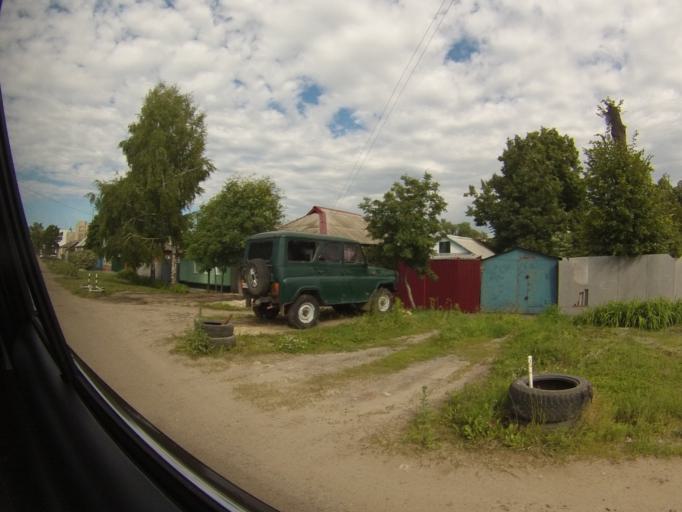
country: RU
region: Orjol
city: Mtsensk
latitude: 53.2762
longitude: 36.5679
